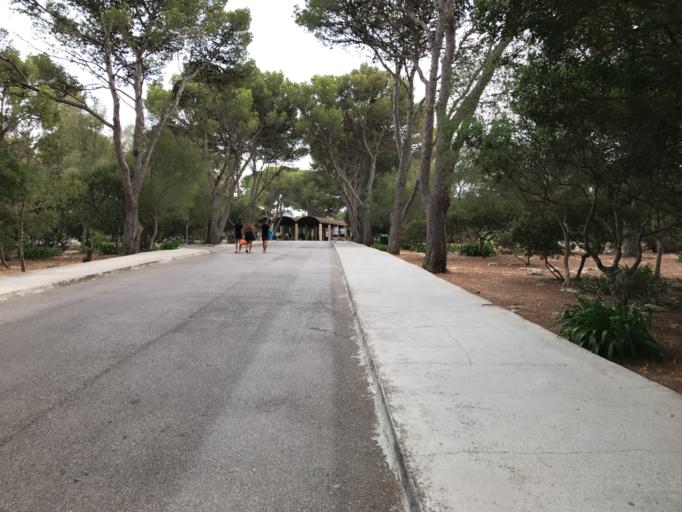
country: ES
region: Balearic Islands
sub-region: Illes Balears
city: Sant Llorenc des Cardassar
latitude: 39.5345
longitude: 3.3307
